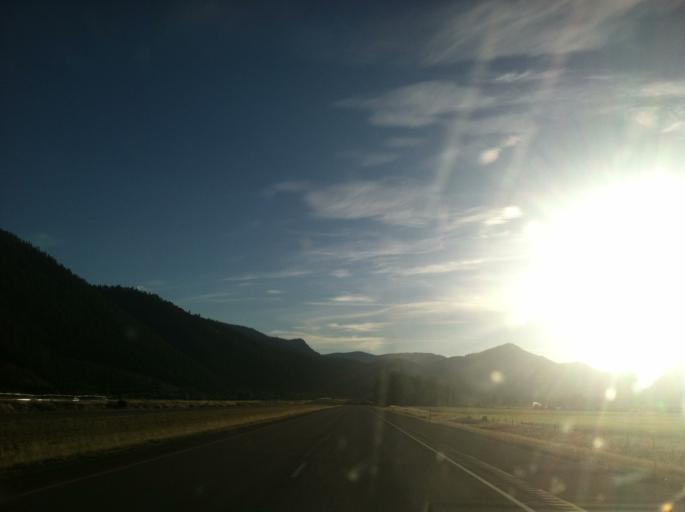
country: US
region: Montana
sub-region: Missoula County
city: Clinton
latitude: 46.7027
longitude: -113.3833
